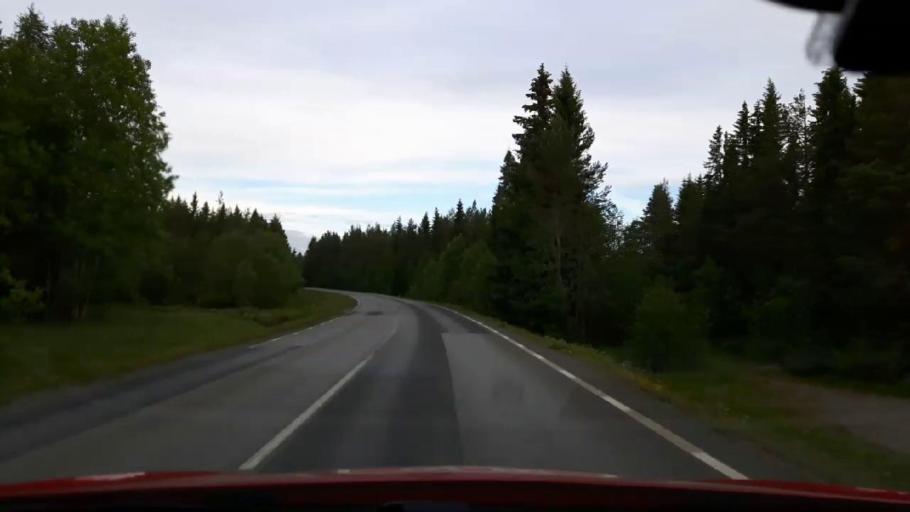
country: SE
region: Jaemtland
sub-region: OEstersunds Kommun
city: Ostersund
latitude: 63.0739
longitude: 14.4445
